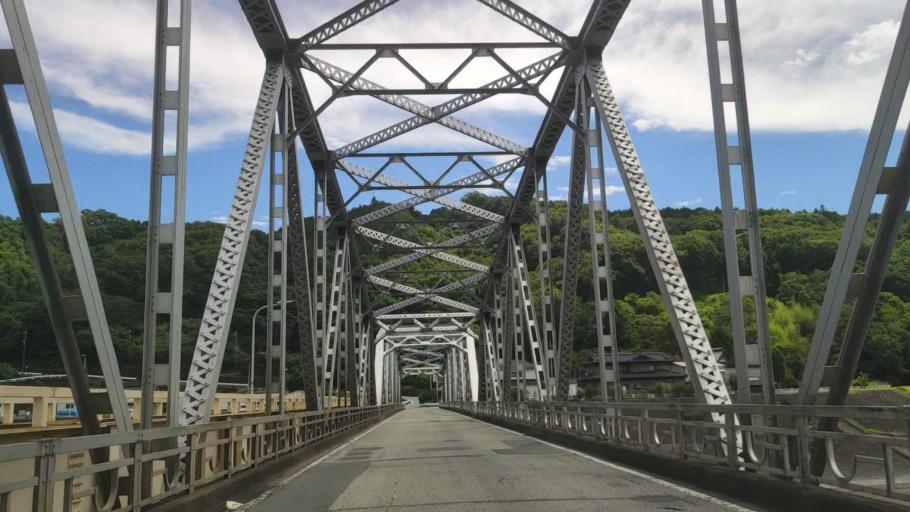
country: JP
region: Yamanashi
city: Ryuo
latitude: 35.5396
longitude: 138.4596
